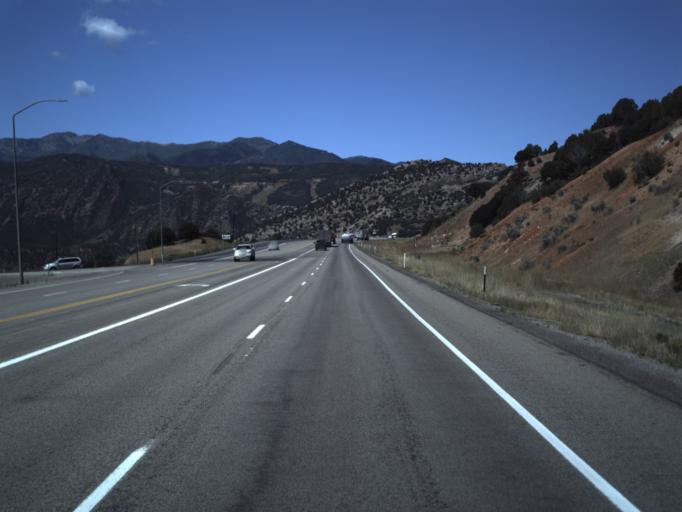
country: US
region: Utah
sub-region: Utah County
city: Mapleton
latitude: 39.9955
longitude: -111.4676
